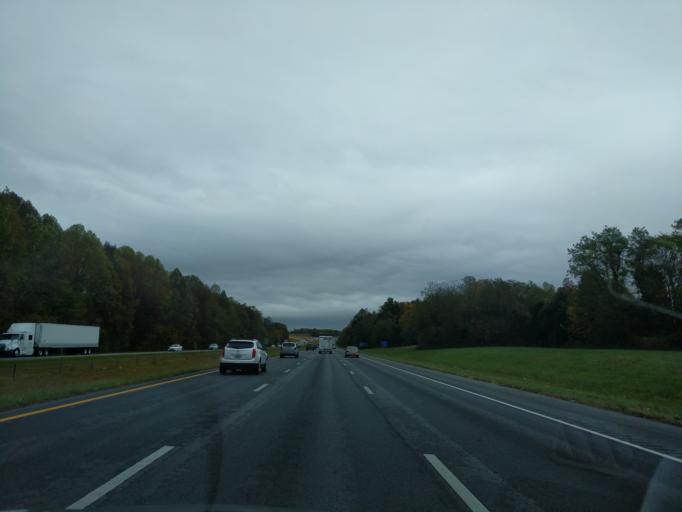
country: US
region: North Carolina
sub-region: Davidson County
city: Thomasville
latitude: 35.8611
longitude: -80.0481
